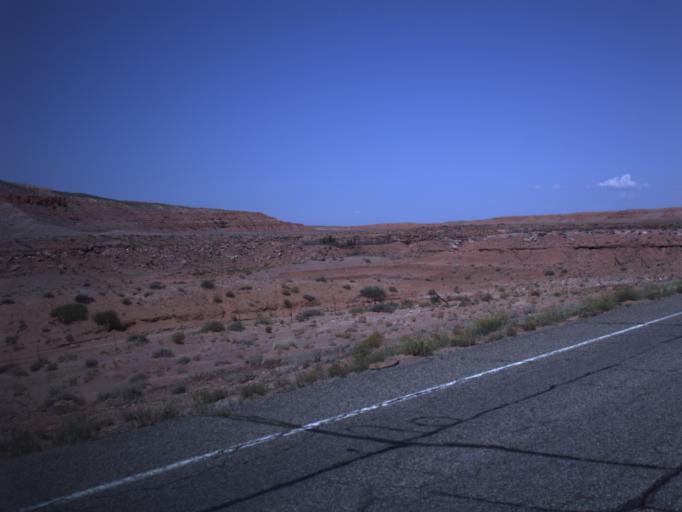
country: US
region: Utah
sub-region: San Juan County
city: Blanding
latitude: 36.9963
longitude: -109.6086
